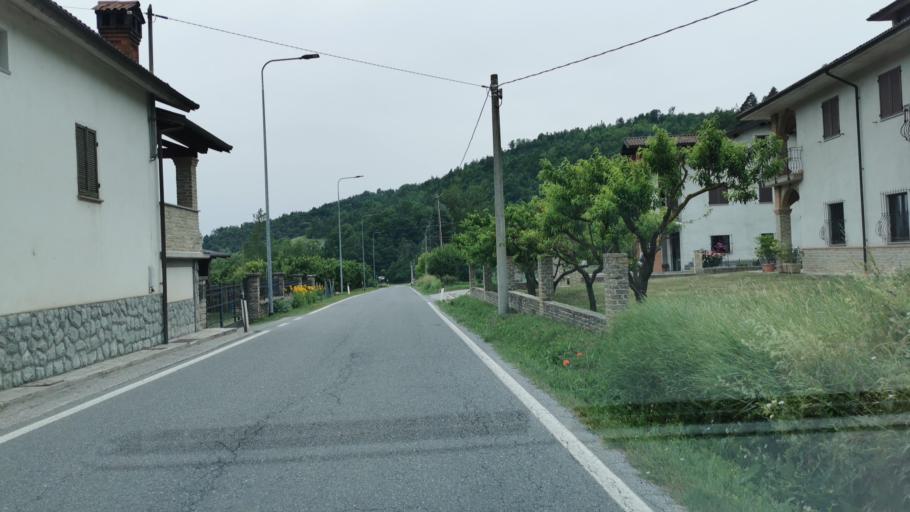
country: IT
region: Piedmont
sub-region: Provincia di Cuneo
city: Torresina
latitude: 44.4173
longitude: 8.0493
